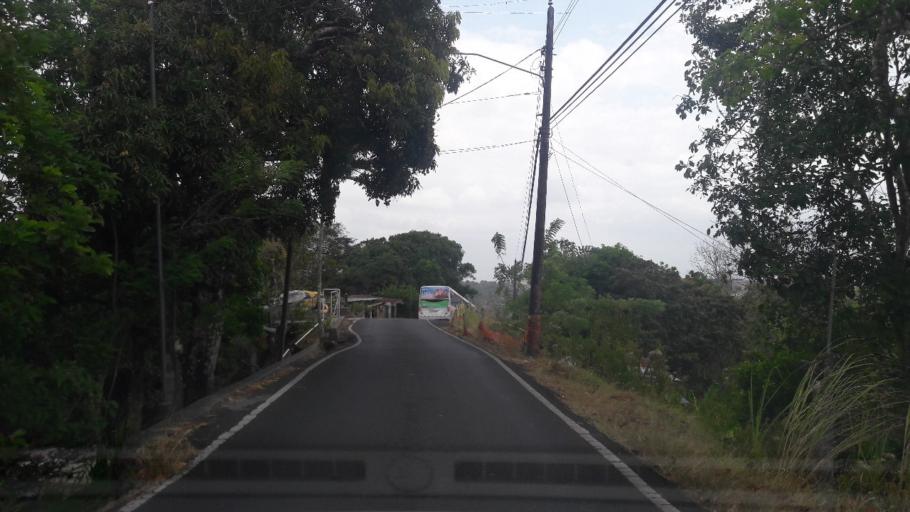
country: PA
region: Panama
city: Alcalde Diaz
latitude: 9.1253
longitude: -79.5533
